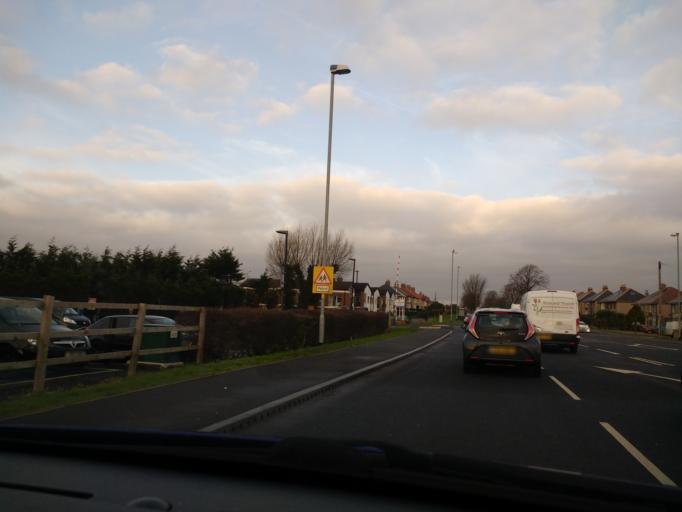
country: GB
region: England
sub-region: Lancashire
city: Morecambe
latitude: 54.0629
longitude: -2.8314
